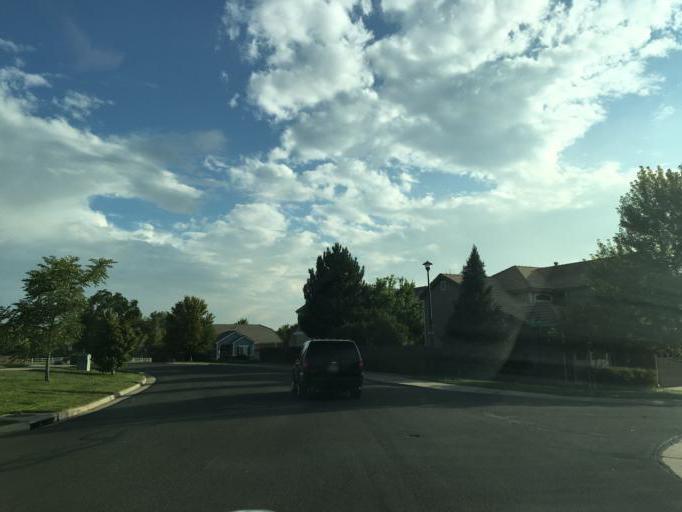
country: US
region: Colorado
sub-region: Adams County
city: Northglenn
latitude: 39.9443
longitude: -104.9545
